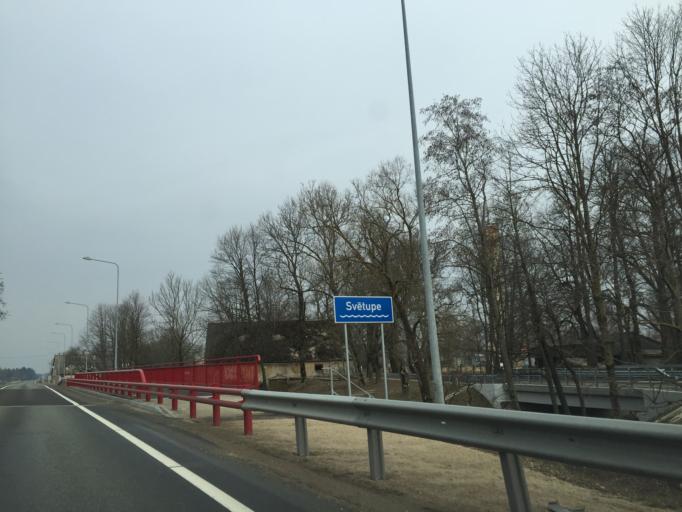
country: LV
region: Salacgrivas
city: Salacgriva
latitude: 57.7005
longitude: 24.3729
